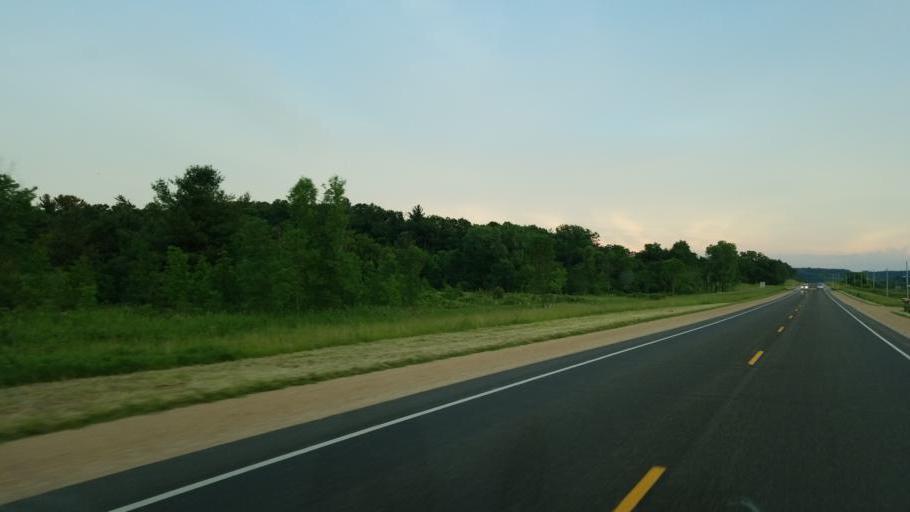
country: US
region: Wisconsin
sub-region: Monroe County
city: Tomah
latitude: 43.8662
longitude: -90.4739
